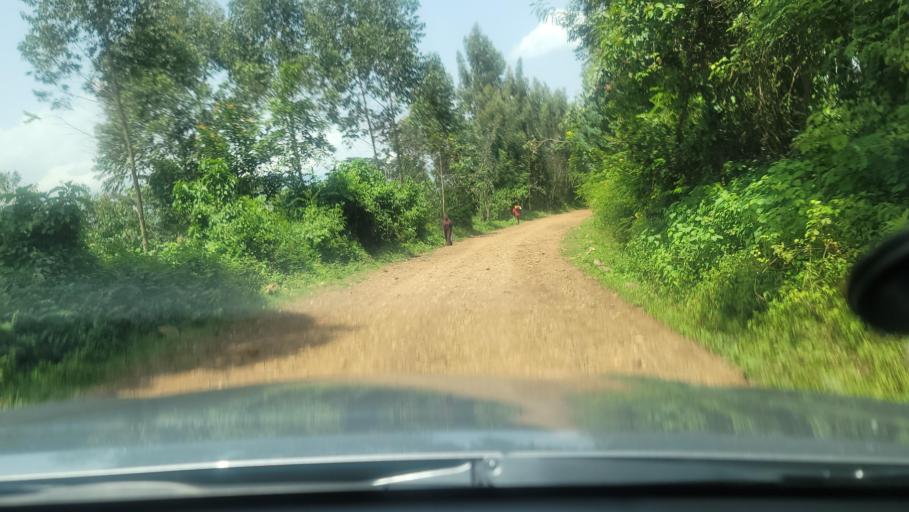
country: ET
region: Oromiya
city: Agaro
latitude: 7.8004
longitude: 36.4175
